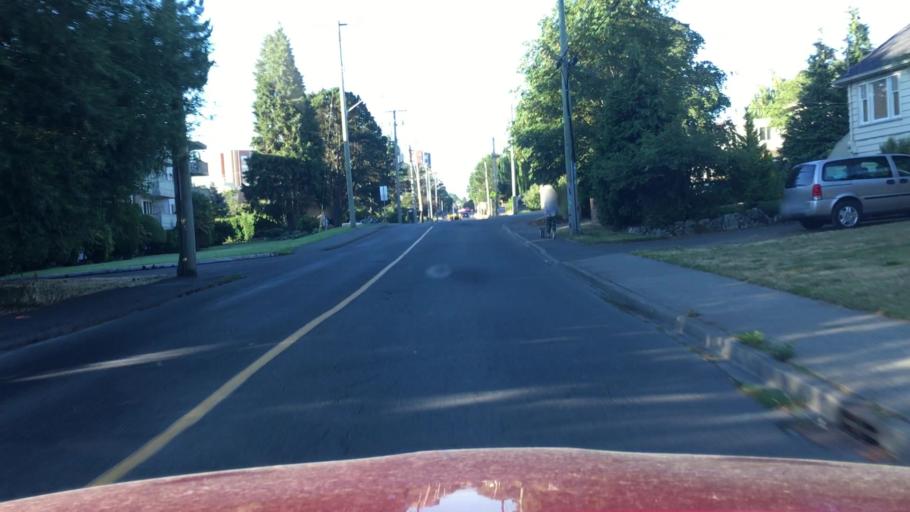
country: CA
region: British Columbia
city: Oak Bay
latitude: 48.4374
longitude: -123.3284
